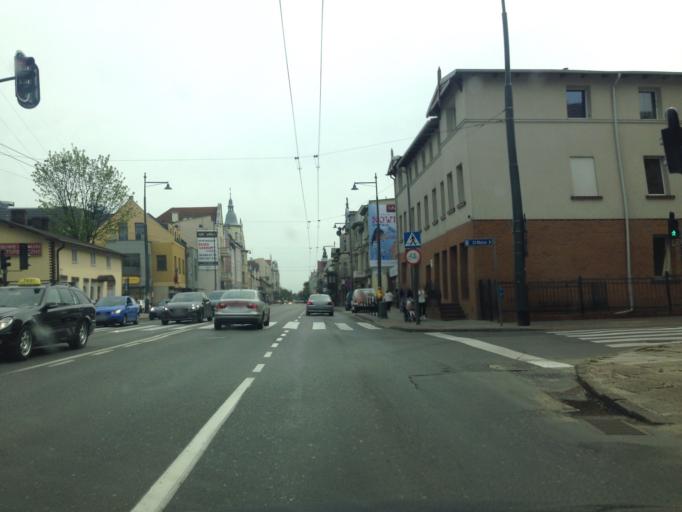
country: PL
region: Pomeranian Voivodeship
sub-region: Sopot
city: Sopot
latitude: 54.4457
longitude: 18.5591
